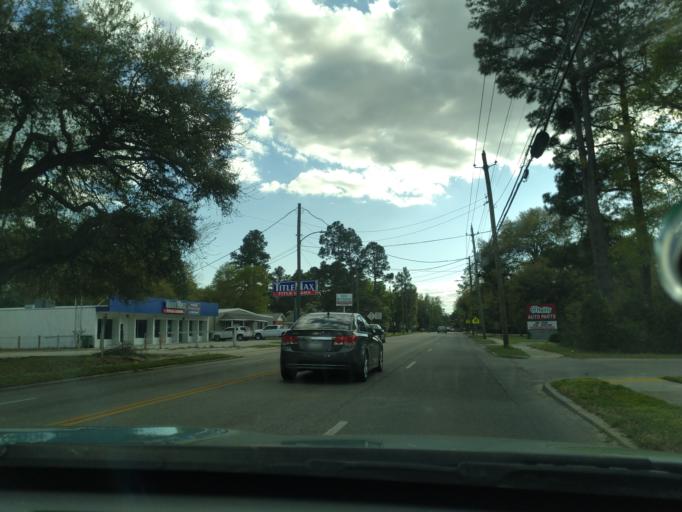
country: US
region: South Carolina
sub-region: Williamsburg County
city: Kingstree
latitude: 33.6784
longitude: -79.8298
